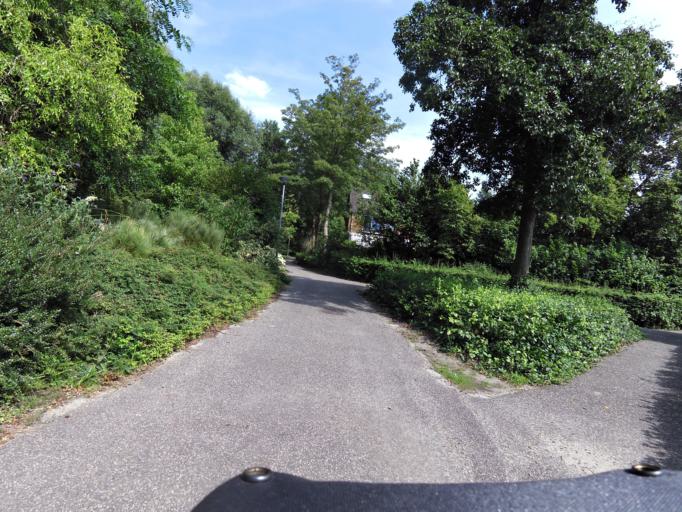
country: NL
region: South Holland
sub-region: Gemeente Goeree-Overflakkee
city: Middelharnis
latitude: 51.7546
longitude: 4.1530
